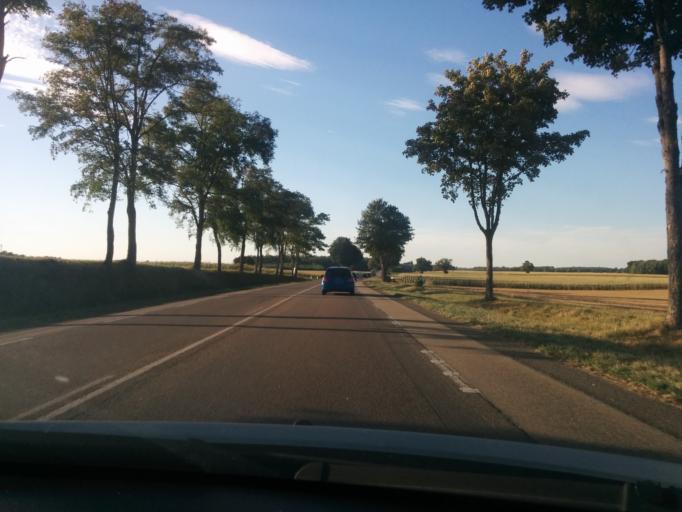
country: FR
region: Rhone-Alpes
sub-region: Departement de l'Ain
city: Tossiat
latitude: 46.1157
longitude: 5.2991
